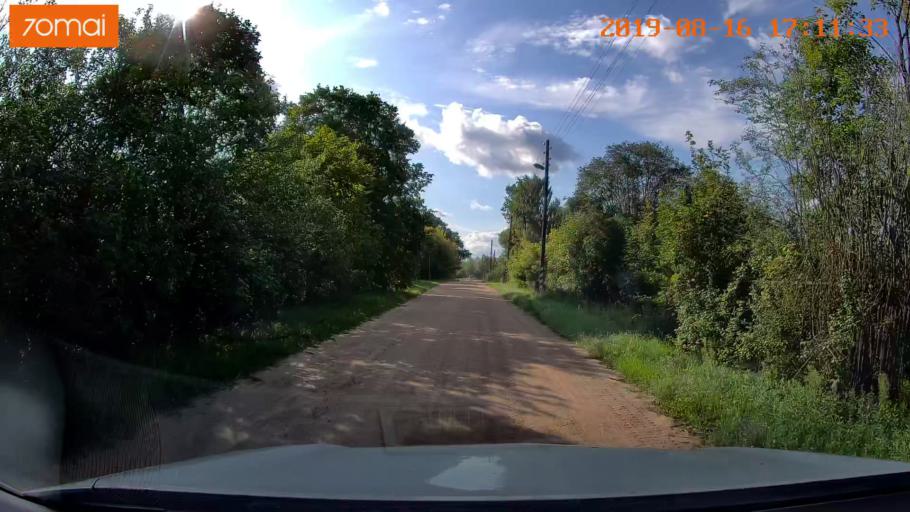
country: BY
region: Mogilev
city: Hlusha
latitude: 53.1959
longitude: 28.9045
